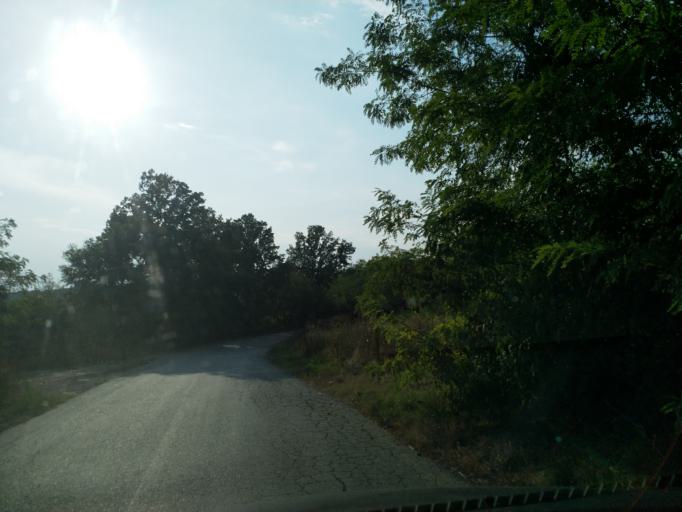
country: RS
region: Central Serbia
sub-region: Pomoravski Okrug
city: Paracin
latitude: 43.8413
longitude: 21.5331
